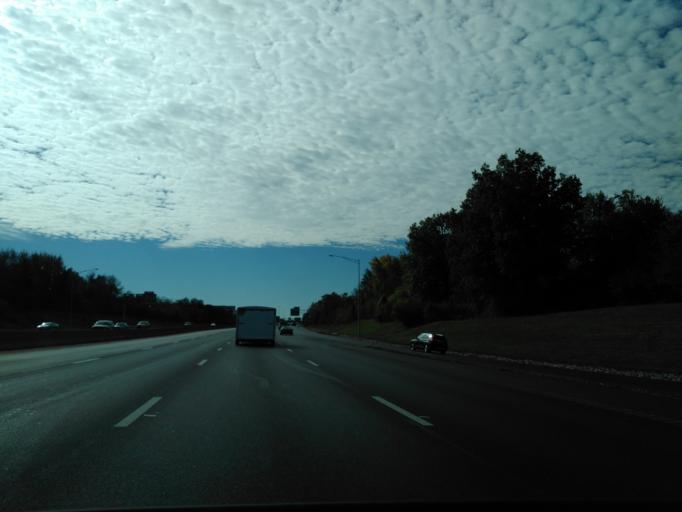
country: US
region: Missouri
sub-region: Saint Louis County
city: Creve Coeur
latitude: 38.6542
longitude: -90.4482
